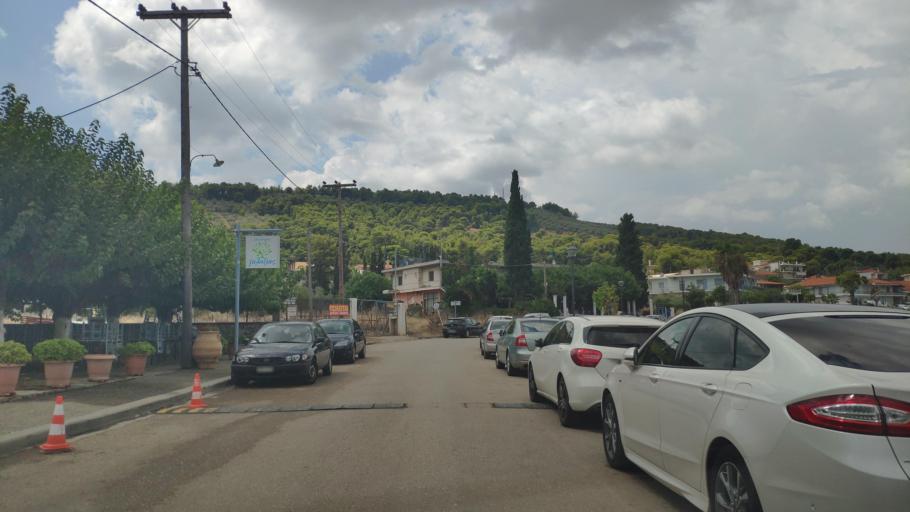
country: GR
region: Central Greece
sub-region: Nomos Fthiotidos
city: Malesina
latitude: 38.6497
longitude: 23.1903
